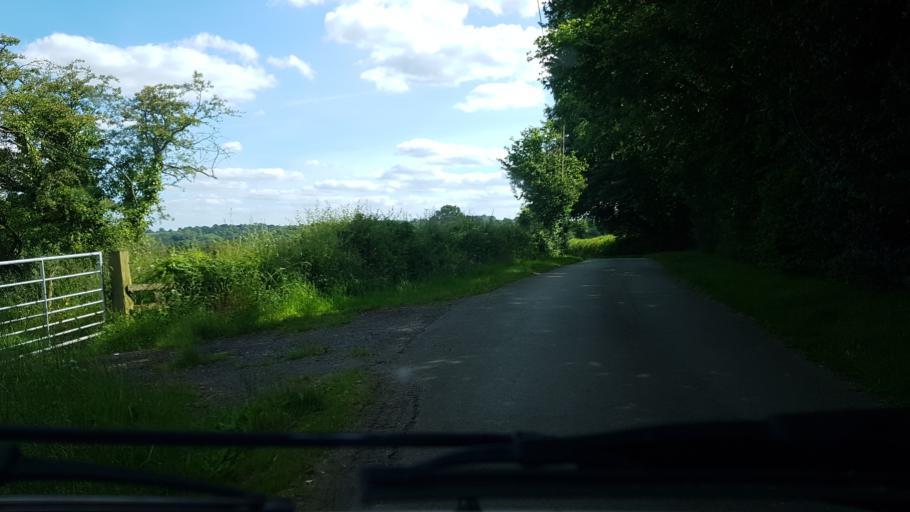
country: GB
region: England
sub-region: Shropshire
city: Romsley
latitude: 52.4451
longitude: -2.3001
